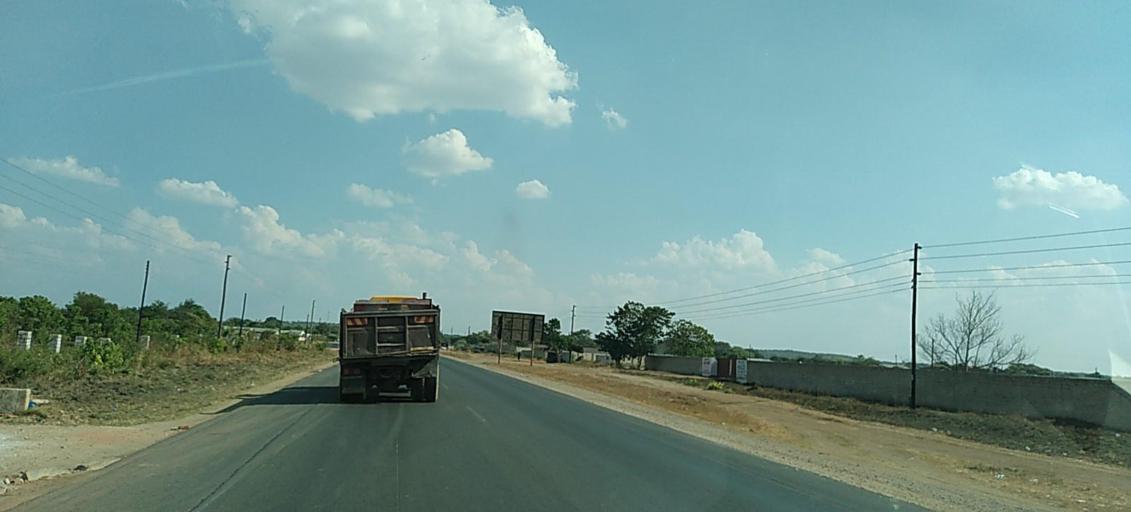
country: ZM
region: Lusaka
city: Lusaka
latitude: -15.2315
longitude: 28.2555
